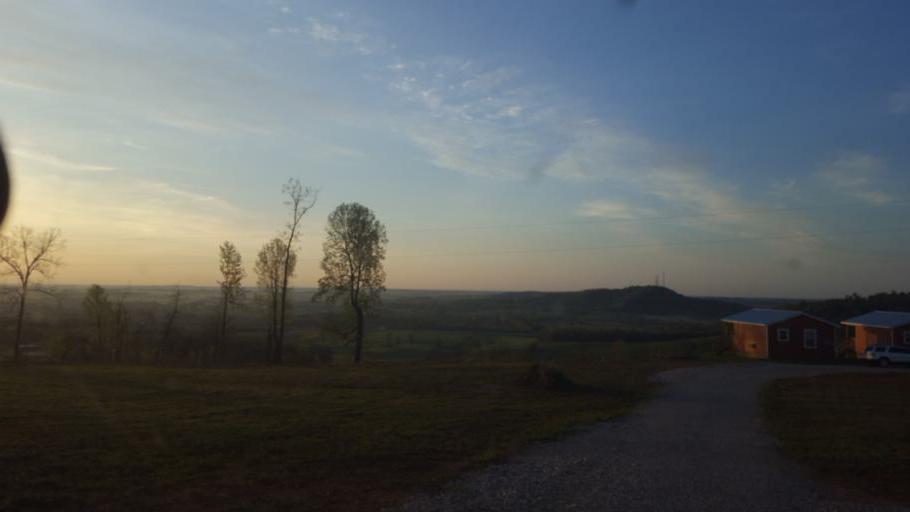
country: US
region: Kentucky
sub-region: Barren County
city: Cave City
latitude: 37.1359
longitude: -86.0003
